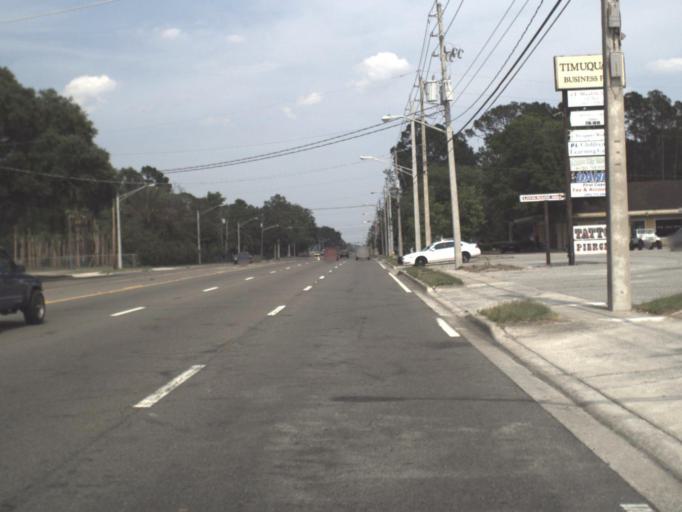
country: US
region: Florida
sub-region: Clay County
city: Bellair-Meadowbrook Terrace
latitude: 30.2473
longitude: -81.7287
